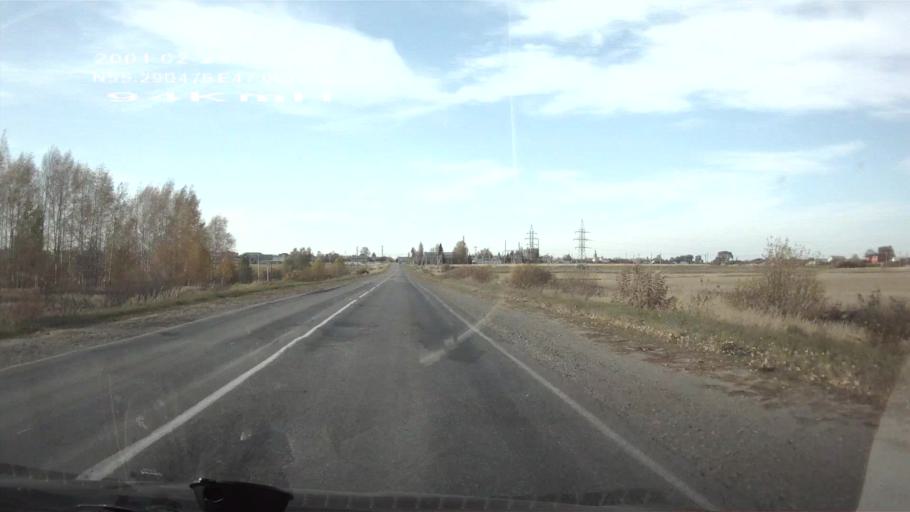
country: RU
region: Chuvashia
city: Ibresi
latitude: 55.2905
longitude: 47.0609
